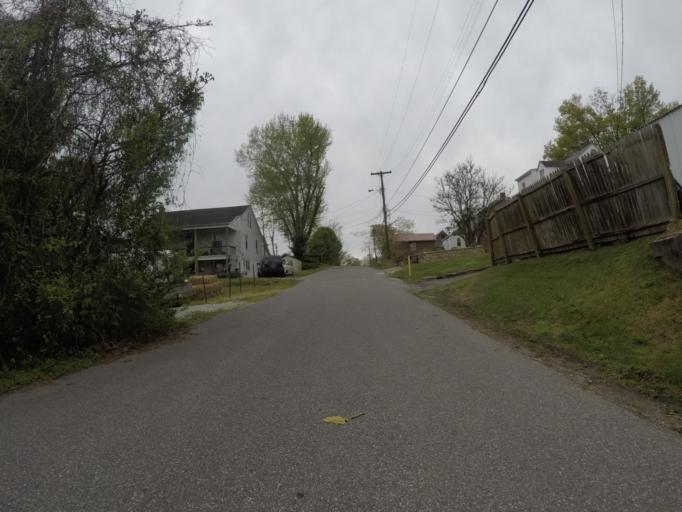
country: US
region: West Virginia
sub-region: Cabell County
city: Huntington
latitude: 38.4093
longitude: -82.3933
